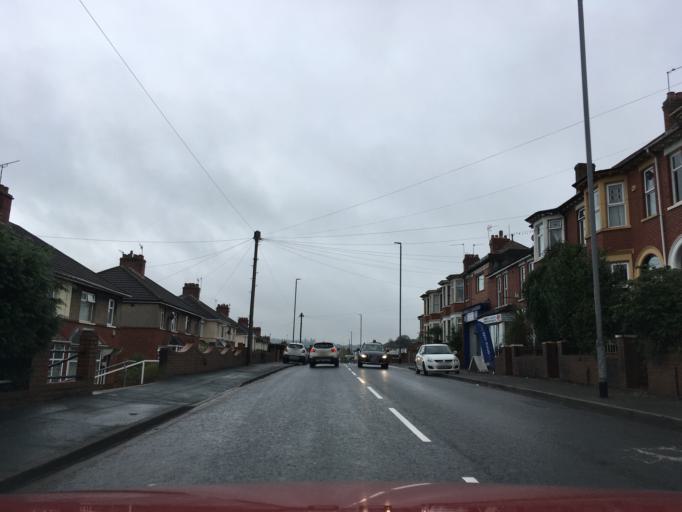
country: GB
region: Wales
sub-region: Newport
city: Caerleon
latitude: 51.6039
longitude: -2.9744
